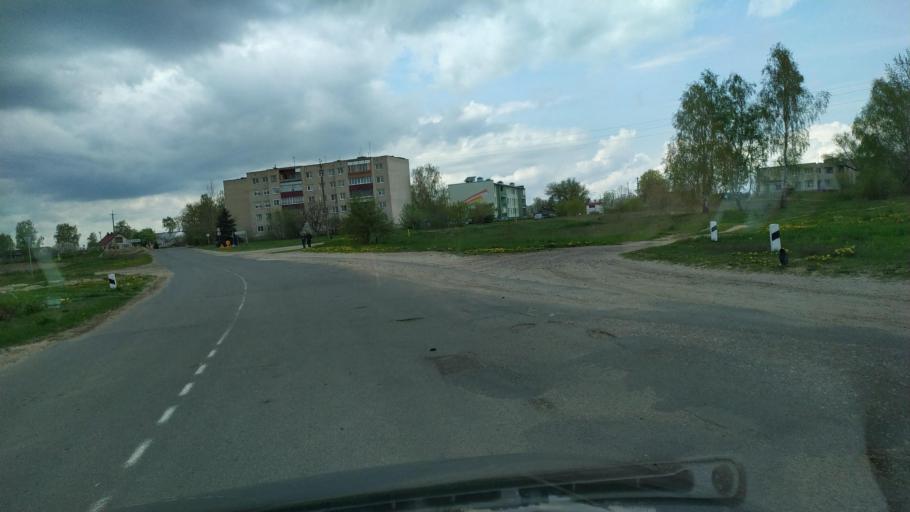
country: BY
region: Brest
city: Pruzhany
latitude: 52.5642
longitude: 24.4225
